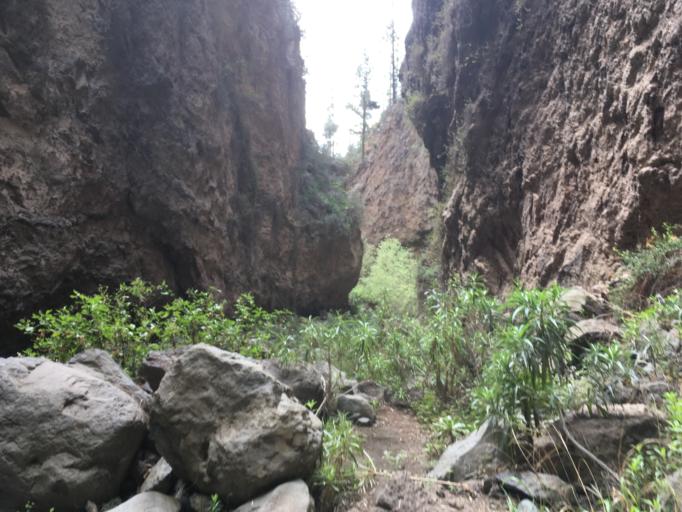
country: ES
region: Canary Islands
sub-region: Provincia de Santa Cruz de Tenerife
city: Vilaflor
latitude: 28.1966
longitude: -16.5741
